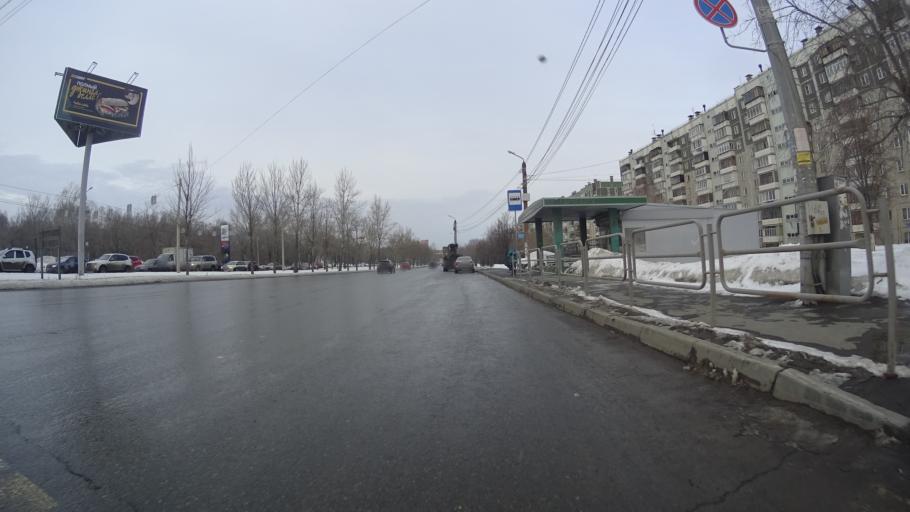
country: RU
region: Chelyabinsk
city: Roshchino
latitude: 55.1791
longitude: 61.2846
